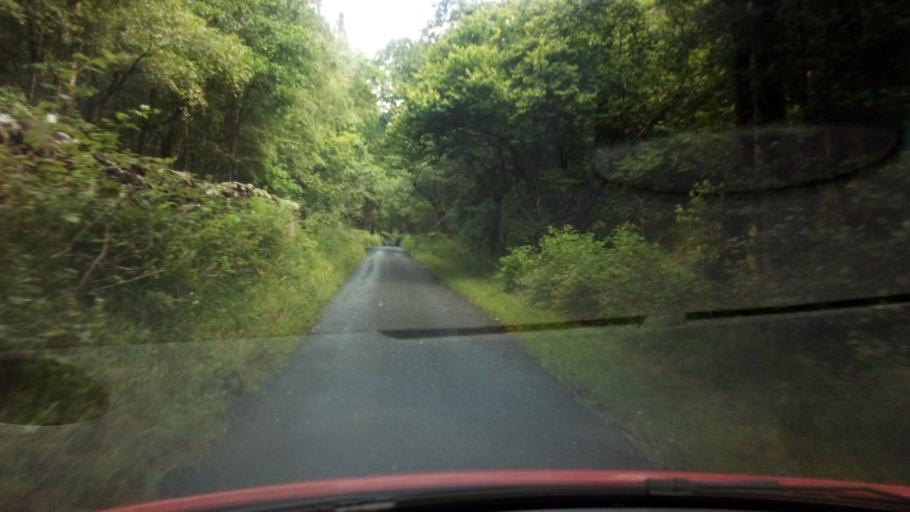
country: GB
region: England
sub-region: Lancashire
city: Clitheroe
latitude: 54.0047
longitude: -2.4089
